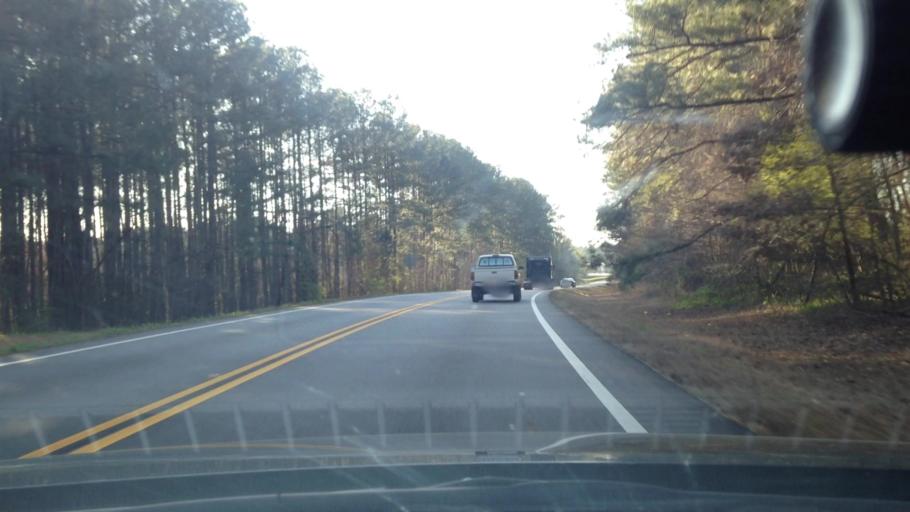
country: US
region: Georgia
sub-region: Fayette County
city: Peachtree City
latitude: 33.3401
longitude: -84.6656
